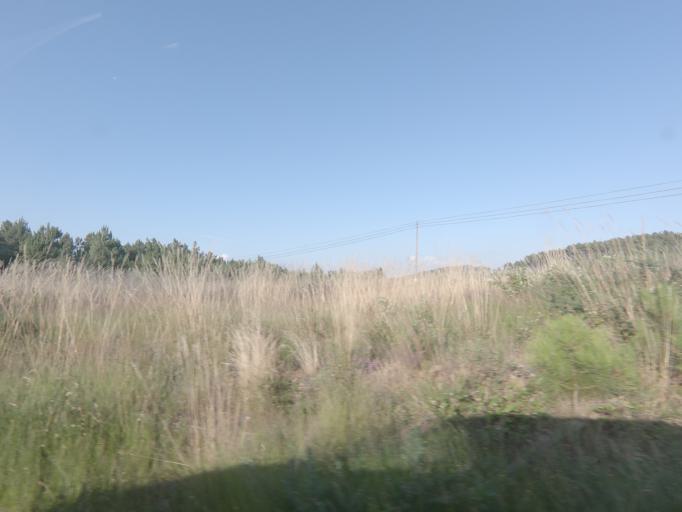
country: PT
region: Vila Real
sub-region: Sabrosa
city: Vilela
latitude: 41.2441
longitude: -7.6040
